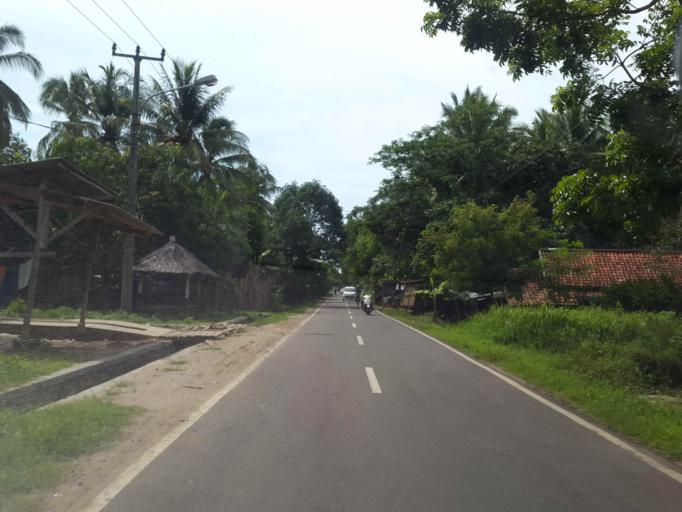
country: ID
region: Banten
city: Citeureup
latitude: -6.5263
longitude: 105.7021
